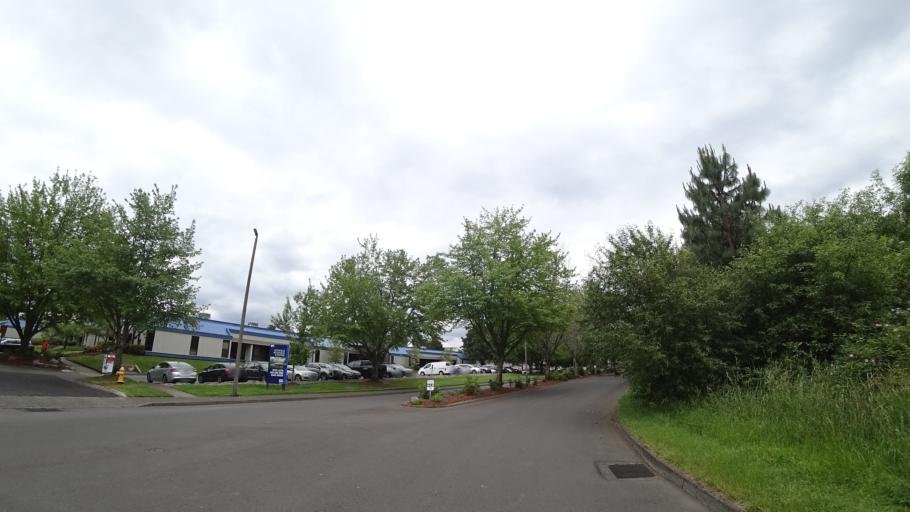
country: US
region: Oregon
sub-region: Washington County
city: Tigard
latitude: 45.4462
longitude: -122.7877
